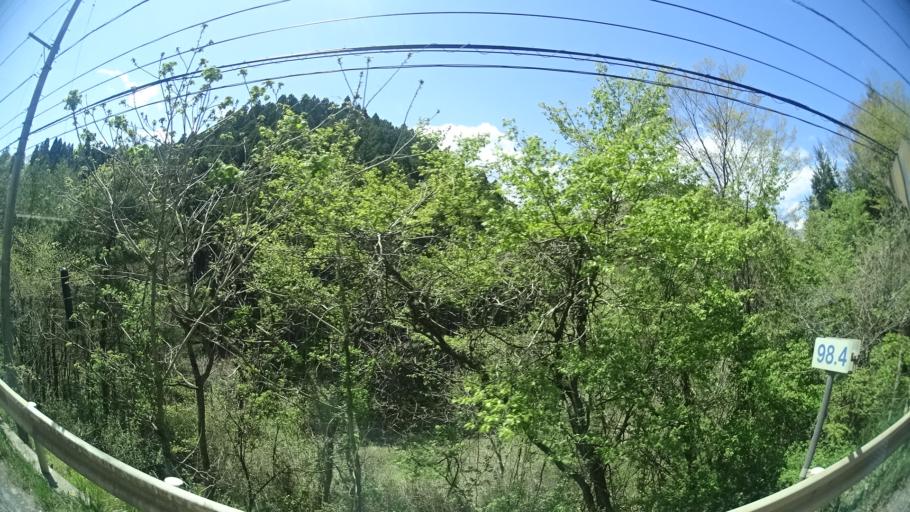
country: JP
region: Miyagi
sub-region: Oshika Gun
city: Onagawa Cho
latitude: 38.6950
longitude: 141.4914
